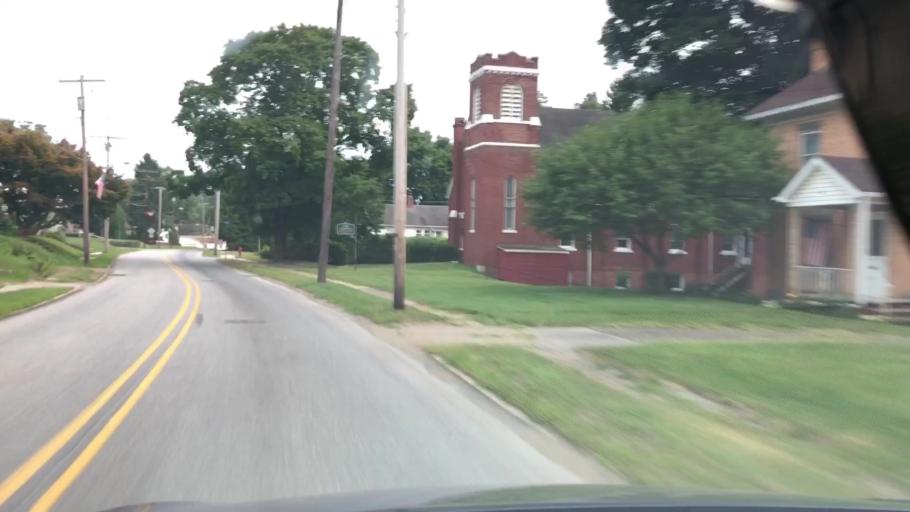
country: US
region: Pennsylvania
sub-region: Venango County
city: Hasson Heights
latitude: 41.4723
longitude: -79.6929
